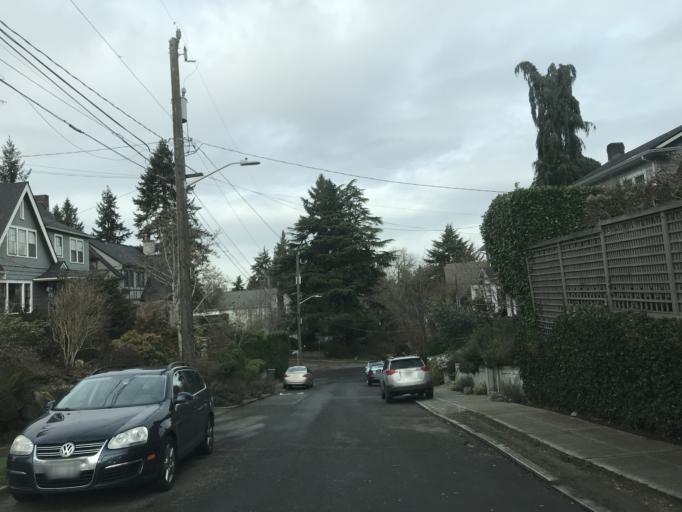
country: US
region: Washington
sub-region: King County
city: Seattle
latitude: 47.6341
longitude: -122.3045
